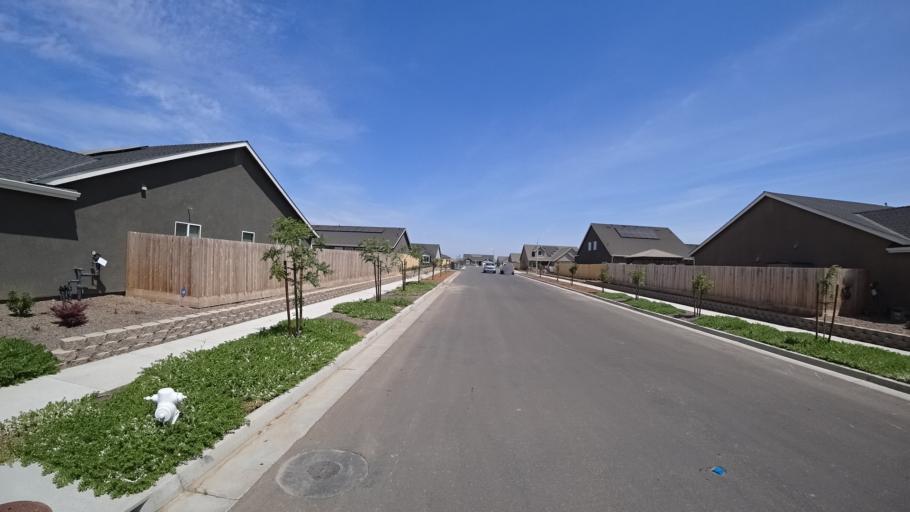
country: US
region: California
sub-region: Kings County
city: Lucerne
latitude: 36.3478
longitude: -119.6854
